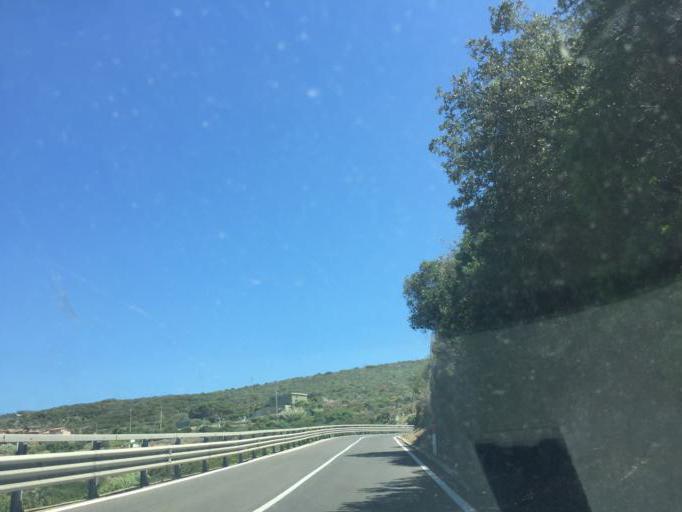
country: IT
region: Sardinia
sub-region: Provincia di Sassari
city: Castelsardo
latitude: 40.9112
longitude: 8.7291
